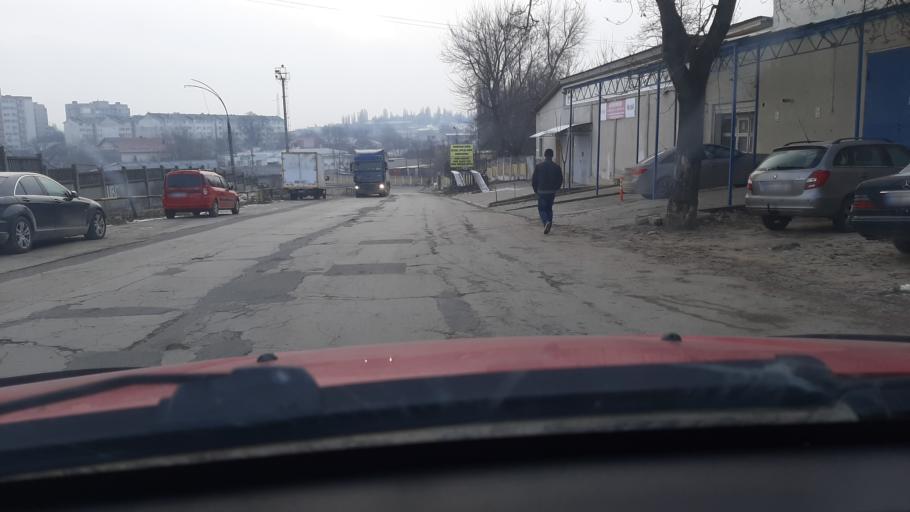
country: MD
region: Chisinau
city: Chisinau
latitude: 46.9852
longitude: 28.8876
